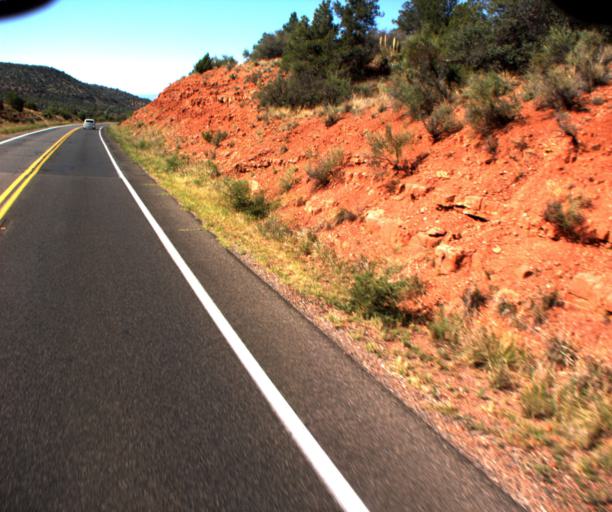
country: US
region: Arizona
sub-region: Yavapai County
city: Big Park
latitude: 34.7514
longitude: -111.7656
